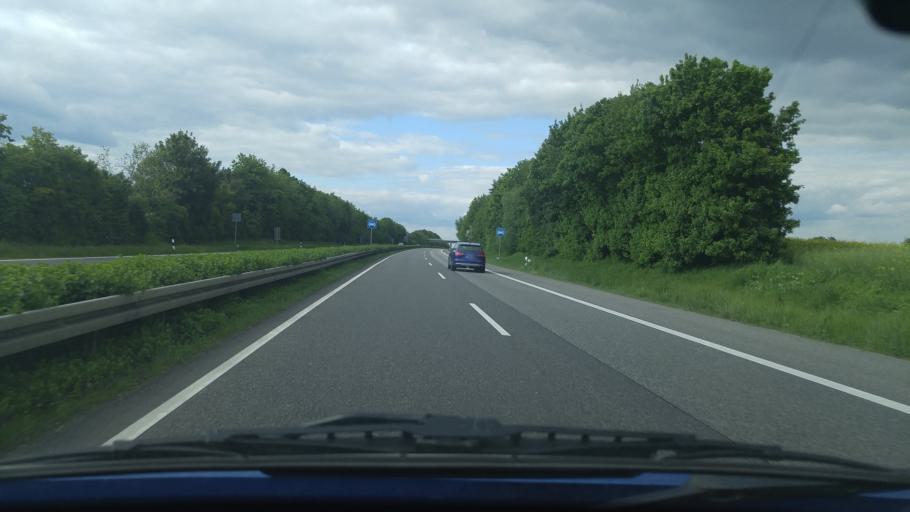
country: DE
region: Hesse
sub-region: Regierungsbezirk Darmstadt
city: Bad Vilbel
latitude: 50.1645
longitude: 8.7022
